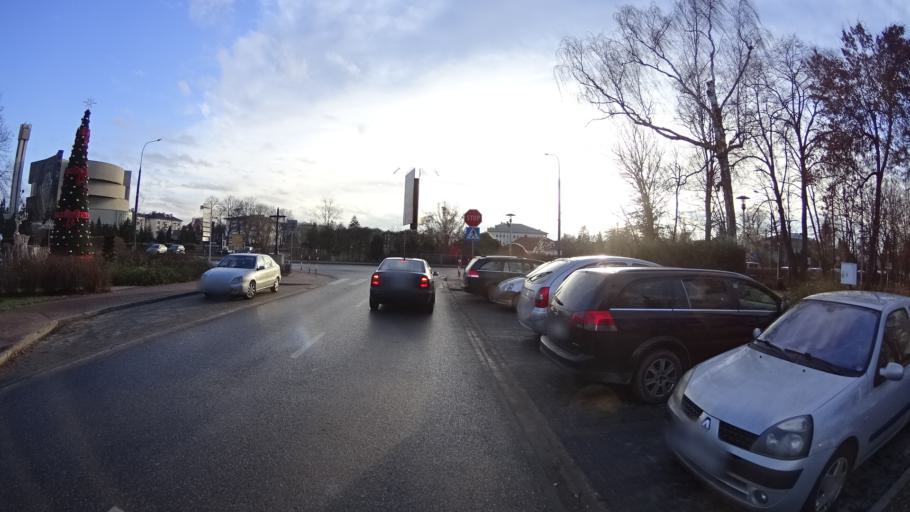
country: PL
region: Masovian Voivodeship
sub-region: Powiat warszawski zachodni
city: Ozarow Mazowiecki
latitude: 52.2108
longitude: 20.7973
